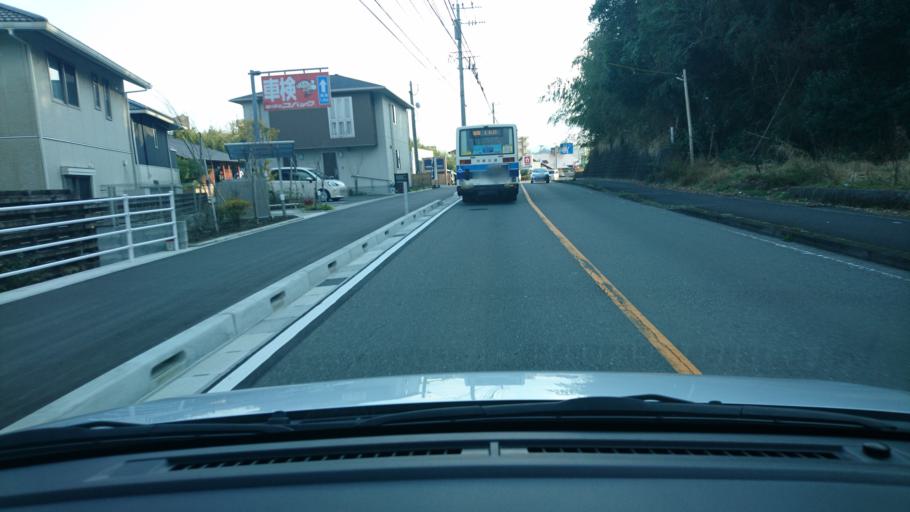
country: JP
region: Miyazaki
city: Miyazaki-shi
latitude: 31.8779
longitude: 131.4057
